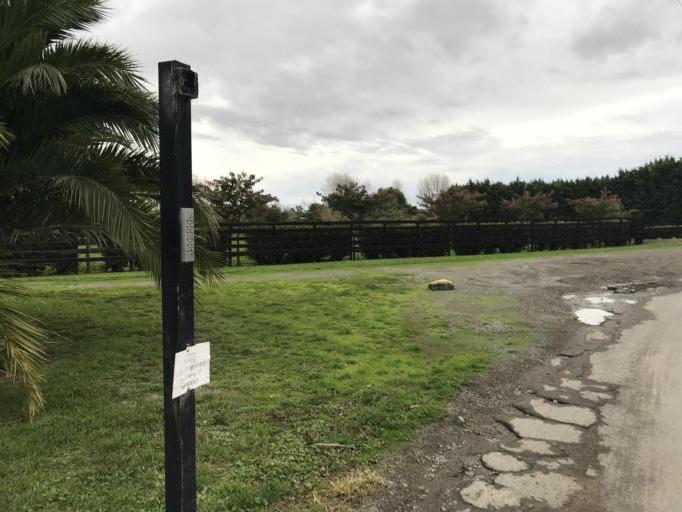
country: NZ
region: Manawatu-Wanganui
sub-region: Palmerston North City
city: Palmerston North
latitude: -40.3809
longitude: 175.5720
